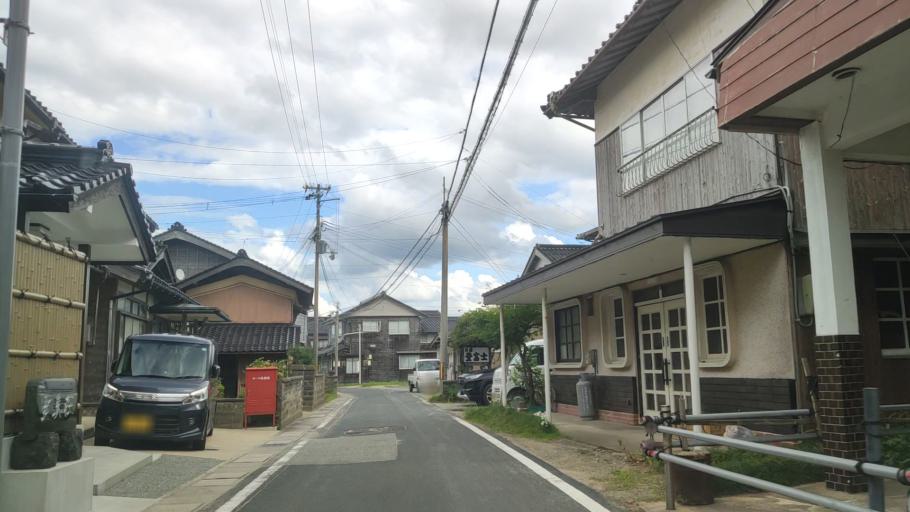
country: JP
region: Hyogo
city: Toyooka
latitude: 35.6425
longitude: 134.9070
